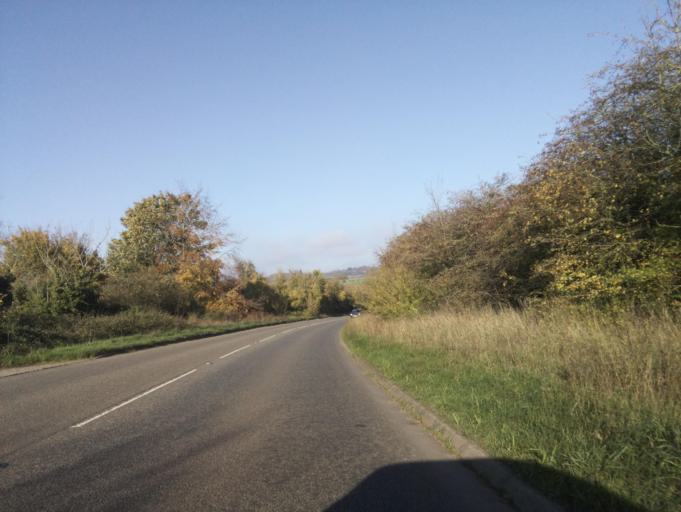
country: GB
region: England
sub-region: Wiltshire
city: Bradford-on-Avon
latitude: 51.3688
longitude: -2.2709
